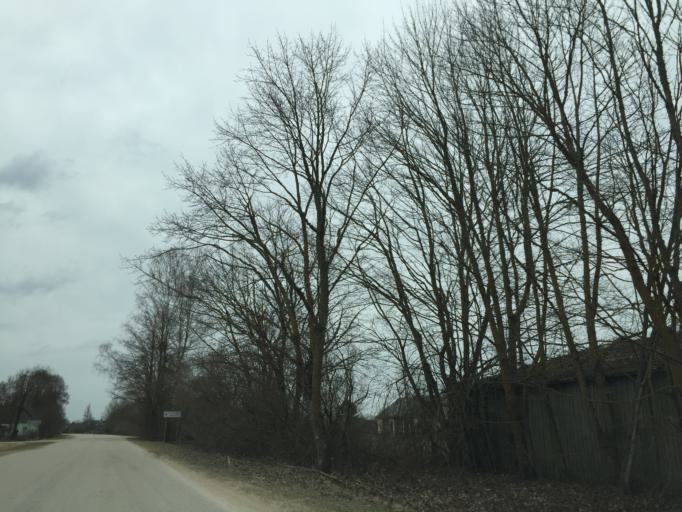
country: LV
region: Livani
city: Livani
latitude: 56.3322
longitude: 26.1604
